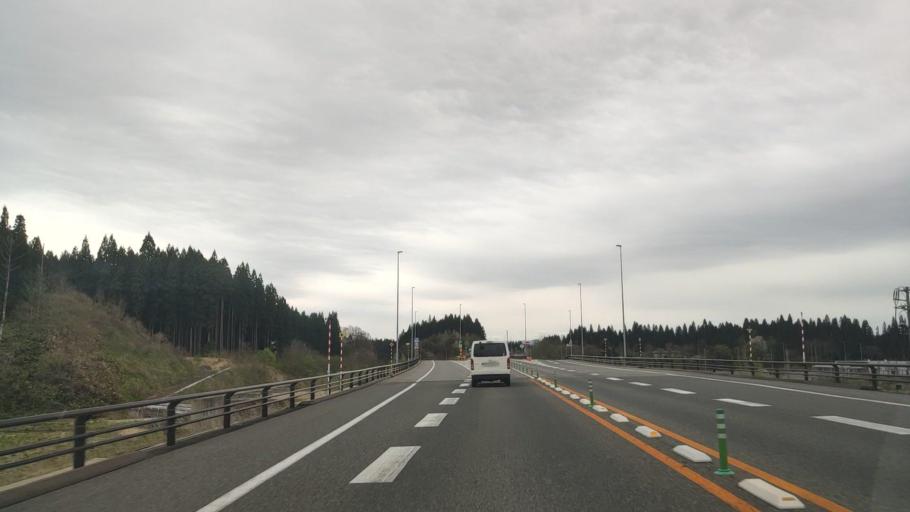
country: JP
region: Akita
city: Odate
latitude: 40.3136
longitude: 140.5796
